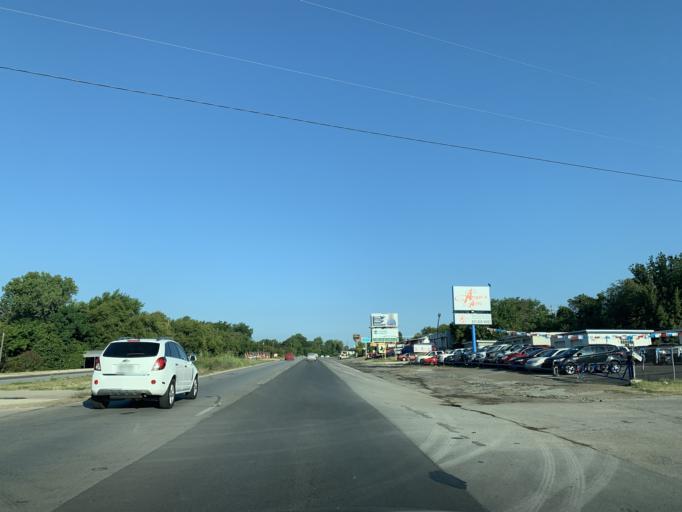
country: US
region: Texas
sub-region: Tarrant County
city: Sansom Park
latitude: 32.7968
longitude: -97.4006
